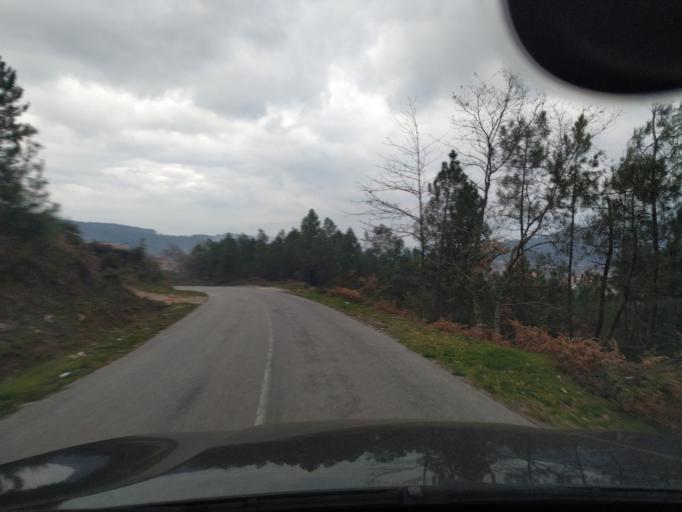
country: PT
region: Vila Real
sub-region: Vila Real
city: Vila Real
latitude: 41.3379
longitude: -7.6589
